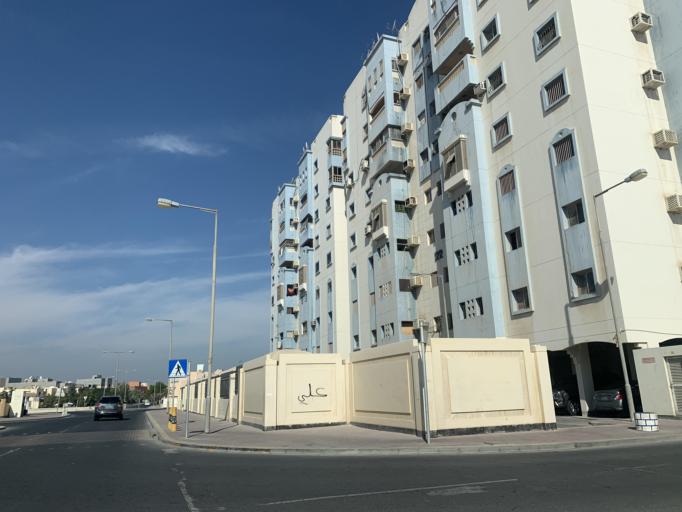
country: BH
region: Central Governorate
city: Madinat Hamad
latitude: 26.1152
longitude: 50.4895
